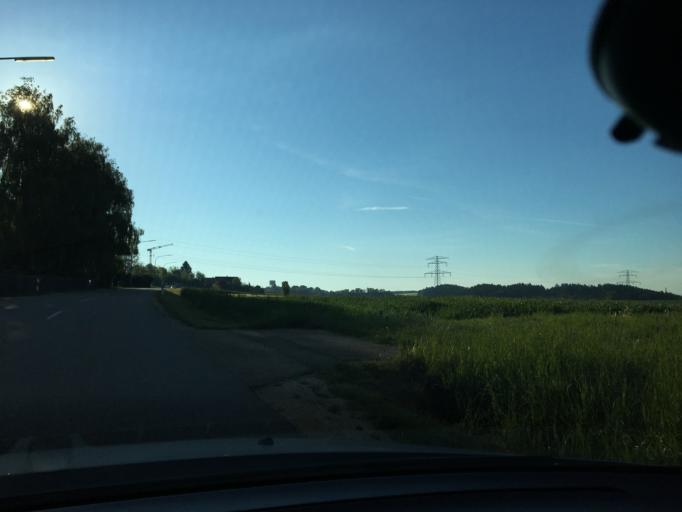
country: DE
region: Bavaria
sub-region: Lower Bavaria
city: Adlkofen
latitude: 48.5219
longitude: 12.3010
